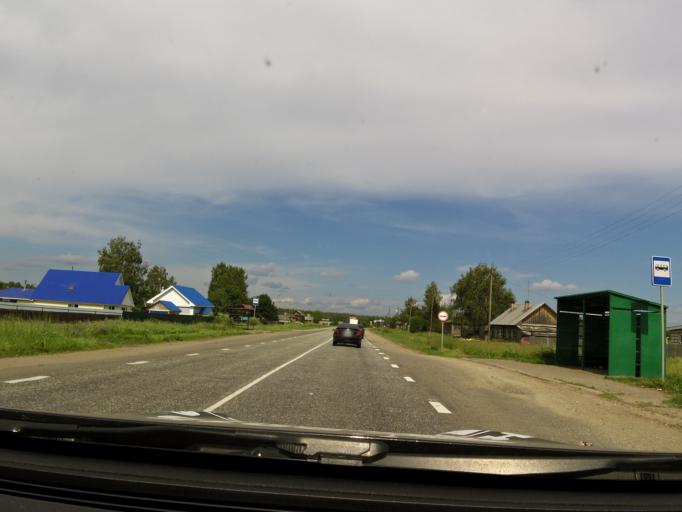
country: RU
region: Kirov
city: Vakhrushi
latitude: 58.6706
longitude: 49.9415
